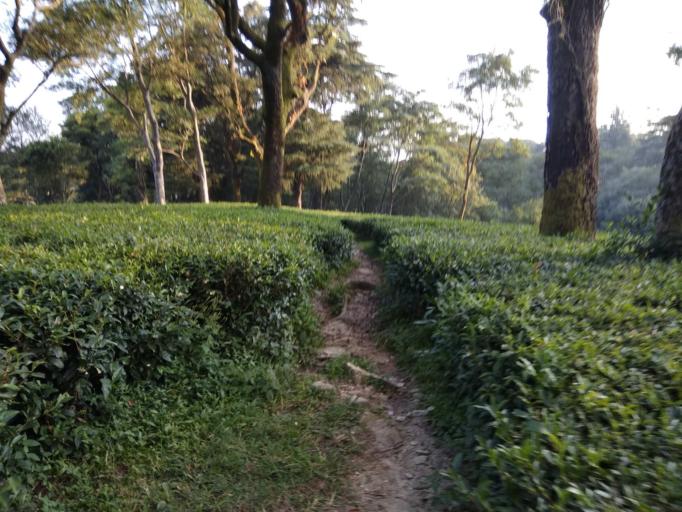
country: IN
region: Himachal Pradesh
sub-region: Kangra
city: Palampur
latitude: 32.1189
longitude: 76.5403
